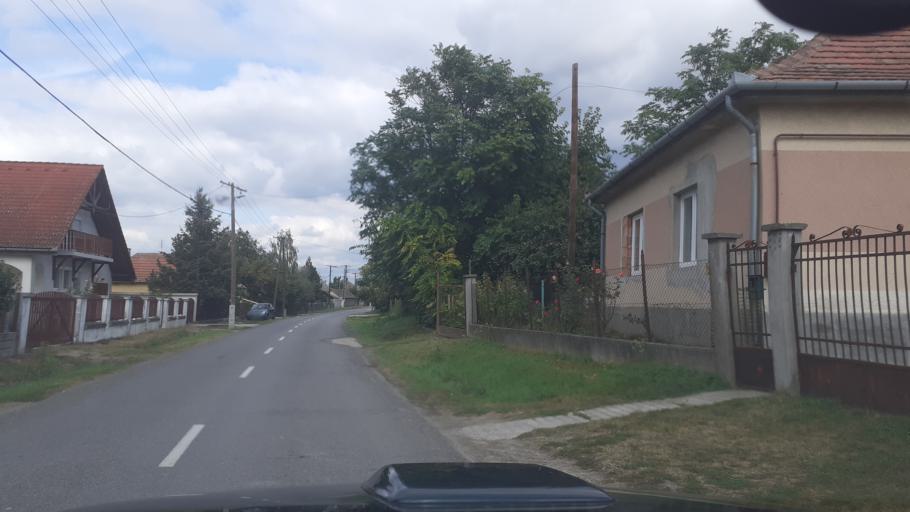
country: HU
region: Bacs-Kiskun
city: Apostag
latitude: 46.8745
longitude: 18.9558
